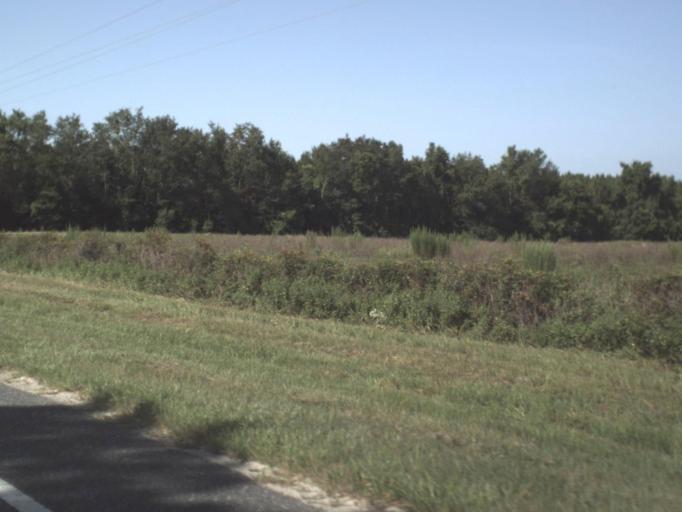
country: US
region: Florida
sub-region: Columbia County
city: Lake City
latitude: 30.0232
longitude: -82.7103
